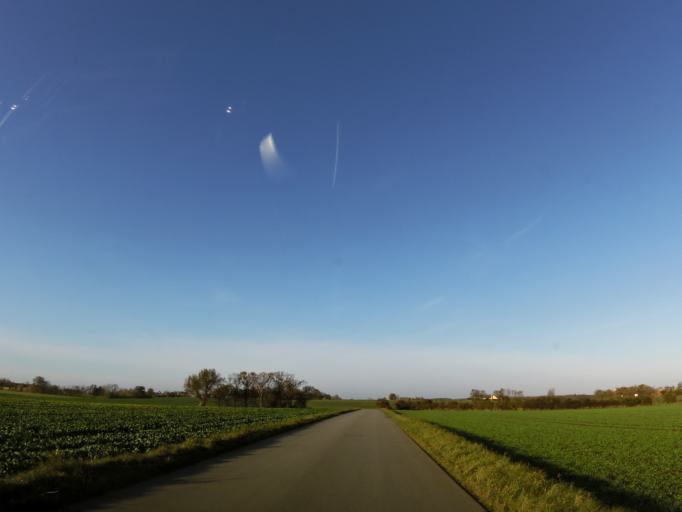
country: DK
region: Central Jutland
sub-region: Arhus Kommune
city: Malling
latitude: 55.9570
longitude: 10.2555
